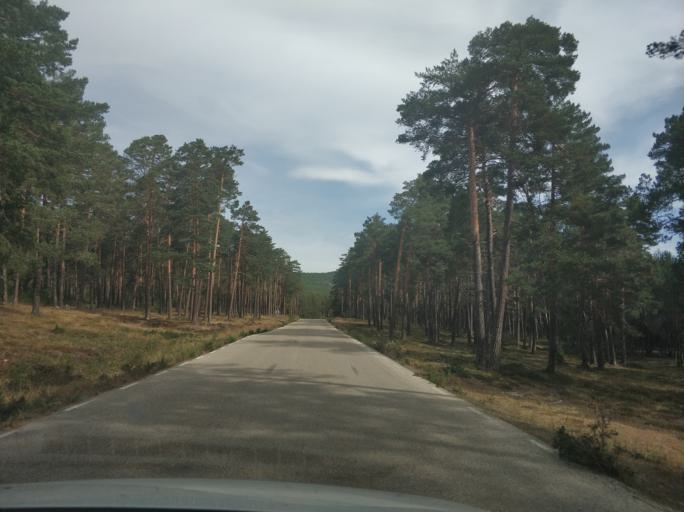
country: ES
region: Castille and Leon
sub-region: Provincia de Soria
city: Navaleno
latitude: 41.8730
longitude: -2.9387
